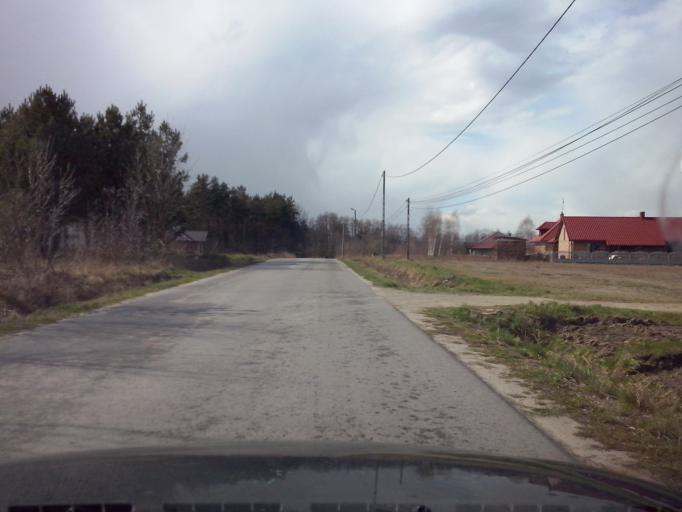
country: PL
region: Subcarpathian Voivodeship
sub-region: Powiat nizanski
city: Krzeszow
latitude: 50.4139
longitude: 22.3422
